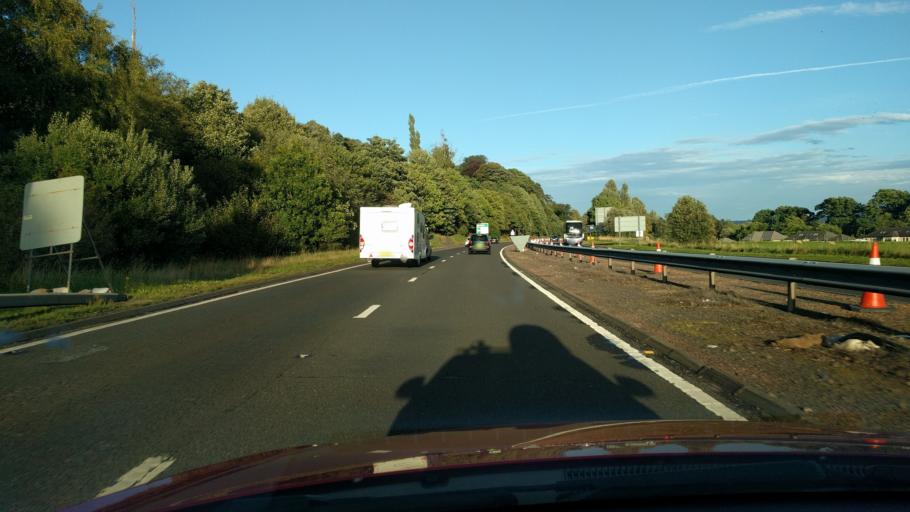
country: GB
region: Scotland
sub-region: Perth and Kinross
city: Scone
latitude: 56.3869
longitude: -3.3913
